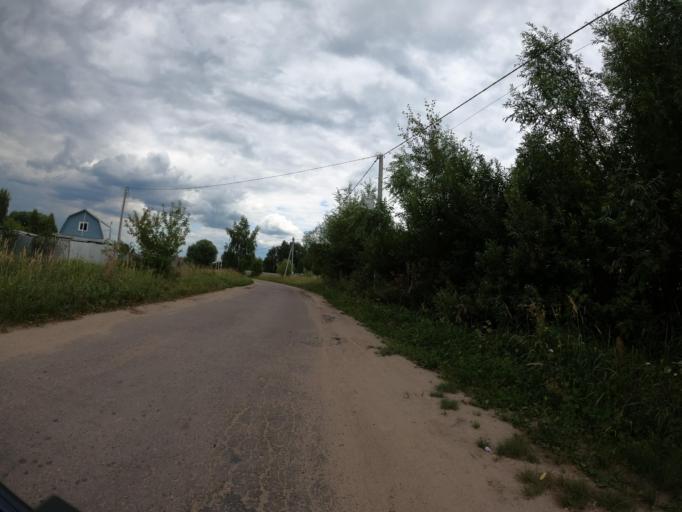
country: RU
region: Moskovskaya
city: Bronnitsy
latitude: 55.4864
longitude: 38.2529
